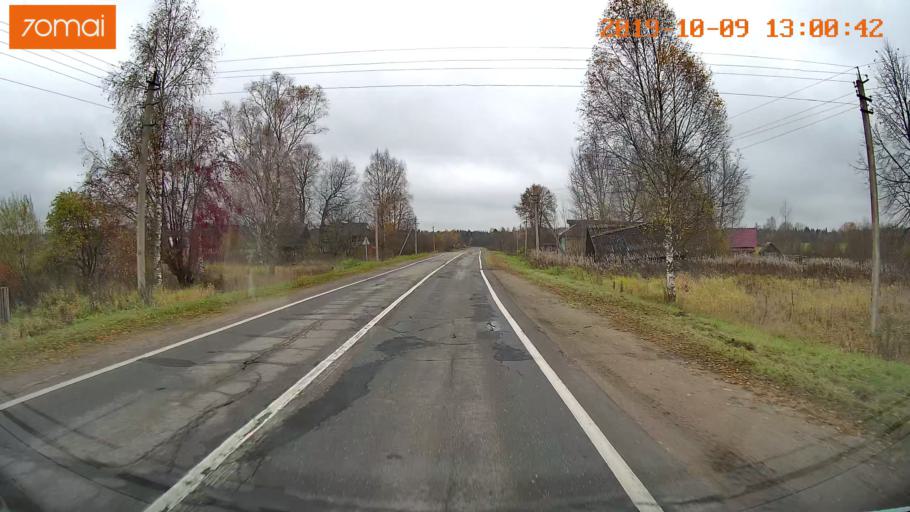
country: RU
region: Jaroslavl
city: Prechistoye
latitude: 58.3747
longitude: 40.4824
